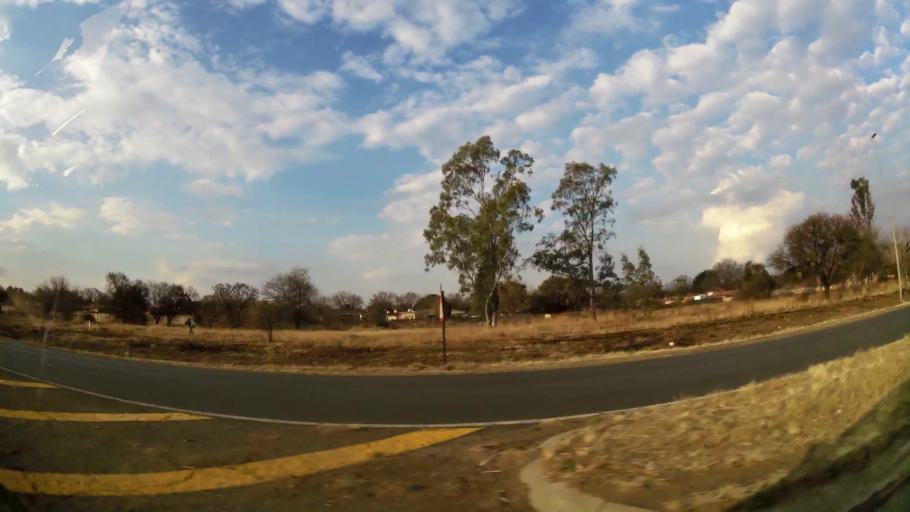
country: ZA
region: Gauteng
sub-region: Sedibeng District Municipality
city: Vanderbijlpark
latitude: -26.7058
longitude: 27.8134
